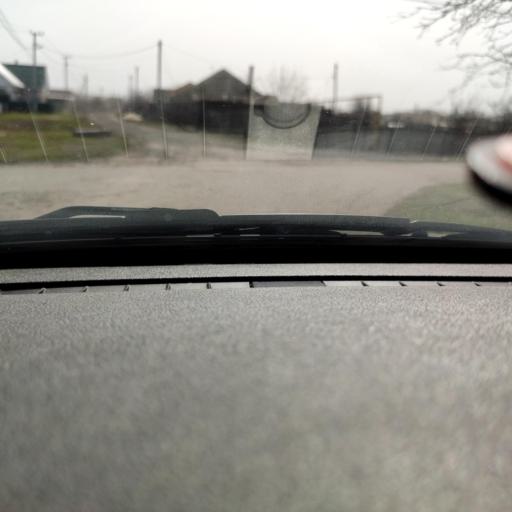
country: RU
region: Voronezj
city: Novaya Usman'
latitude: 51.6296
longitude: 39.4062
